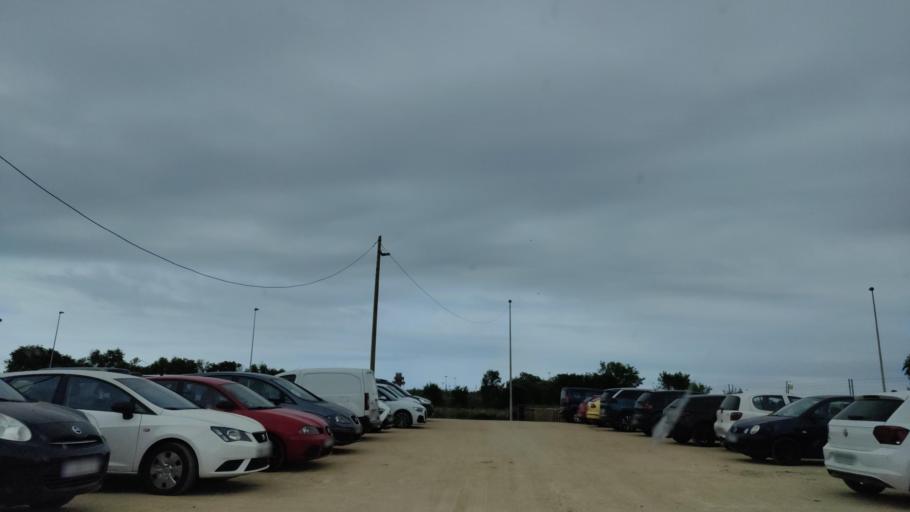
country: ES
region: Catalonia
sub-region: Provincia de Barcelona
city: El Prat de Llobregat
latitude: 41.3145
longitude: 2.0832
